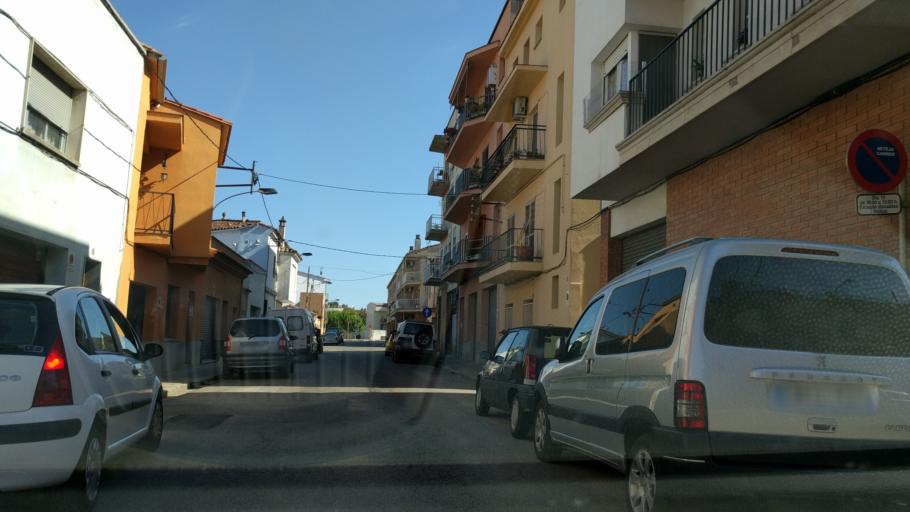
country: ES
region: Catalonia
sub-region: Provincia de Girona
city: Salt
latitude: 41.9736
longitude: 2.7808
